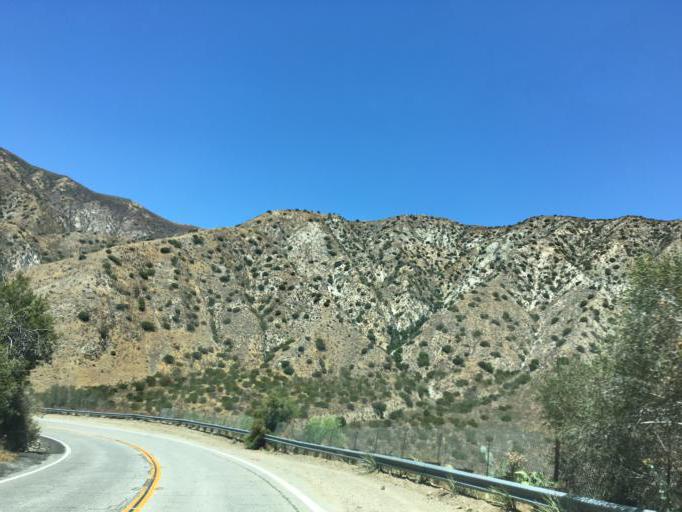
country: US
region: California
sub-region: Los Angeles County
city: La Crescenta-Montrose
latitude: 34.2996
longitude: -118.2757
